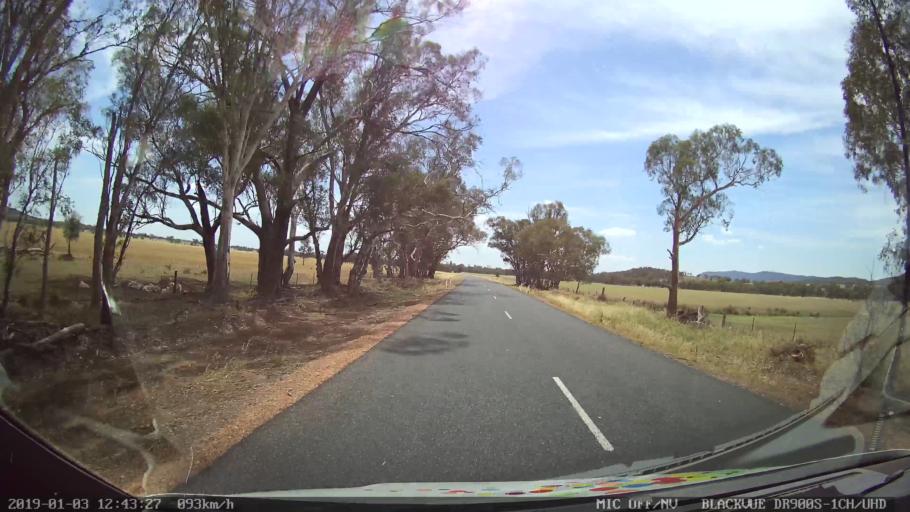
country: AU
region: New South Wales
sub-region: Weddin
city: Grenfell
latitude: -33.7748
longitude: 148.2120
